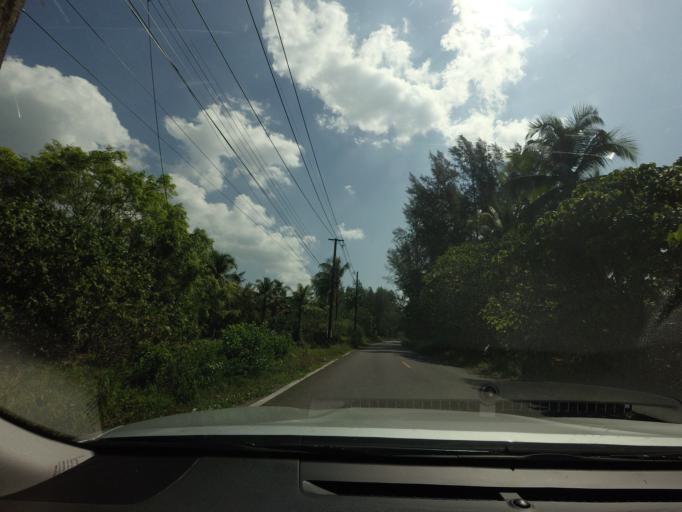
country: TH
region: Phangnga
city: Ban Khao Lak
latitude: 8.7274
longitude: 98.2384
